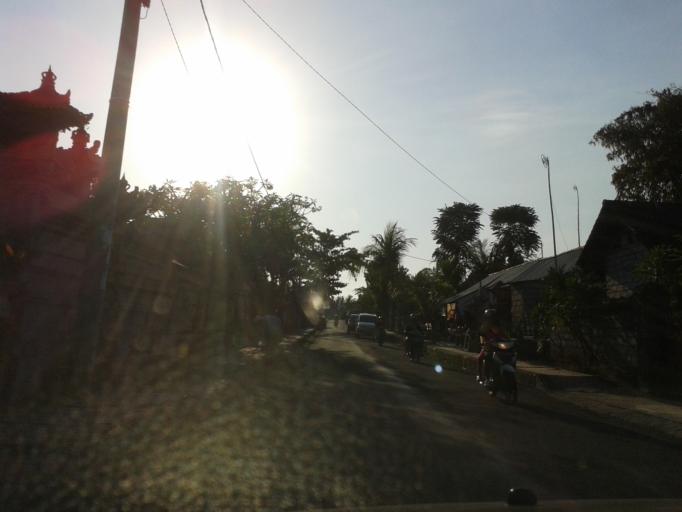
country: ID
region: Bali
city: Semarapura
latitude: -8.5549
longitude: 115.3901
